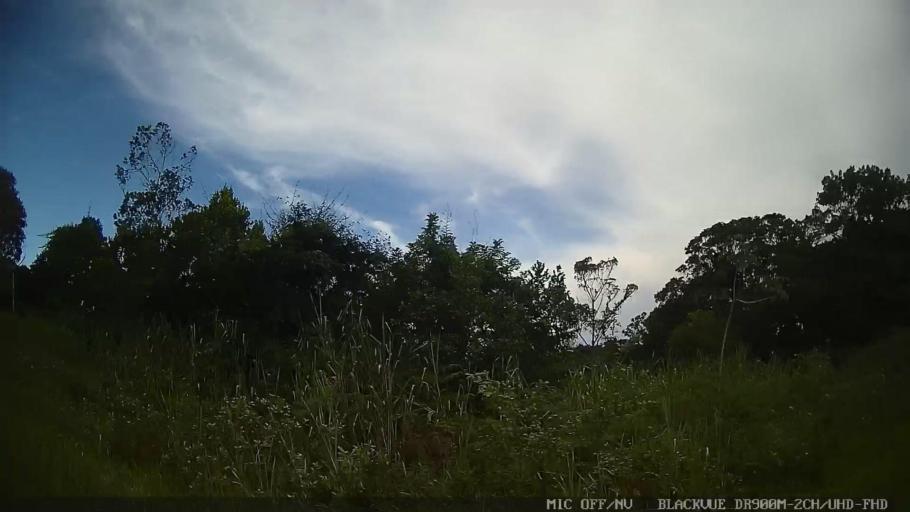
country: BR
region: Sao Paulo
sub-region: Iguape
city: Iguape
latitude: -24.6572
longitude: -47.4106
